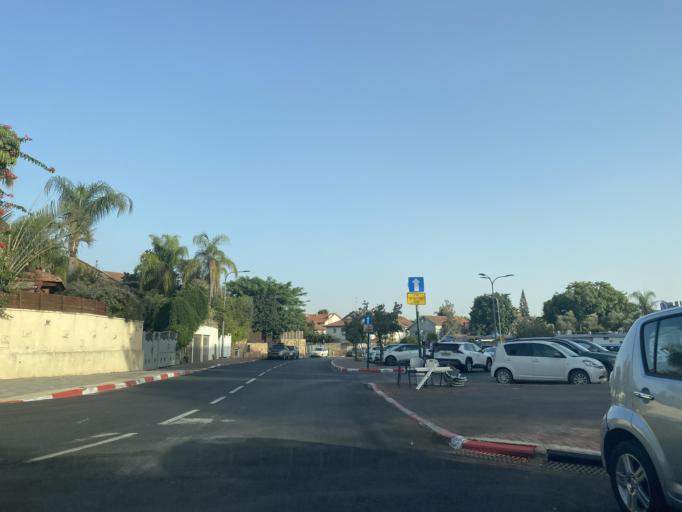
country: IL
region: Central District
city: Hod HaSharon
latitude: 32.1564
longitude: 34.9020
